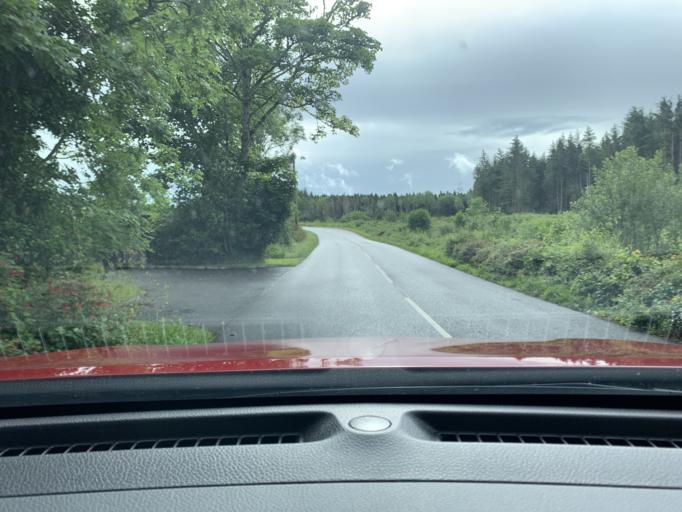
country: GB
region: Northern Ireland
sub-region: Fermanagh District
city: Enniskillen
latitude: 54.2574
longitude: -7.7620
